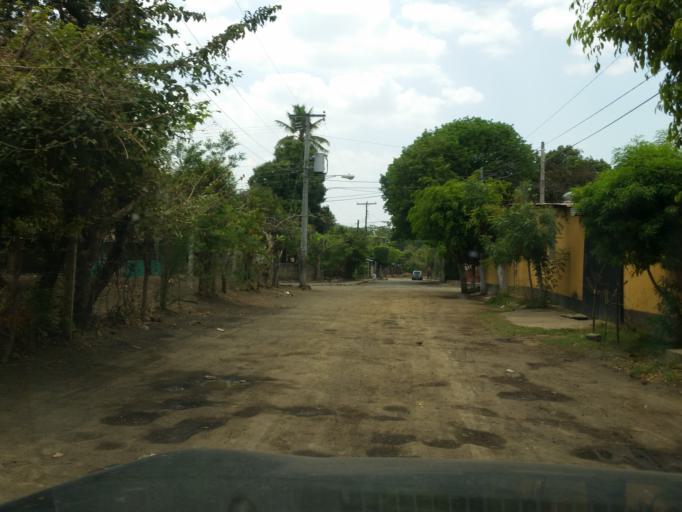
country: NI
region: Managua
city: Managua
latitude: 12.1207
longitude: -86.1647
